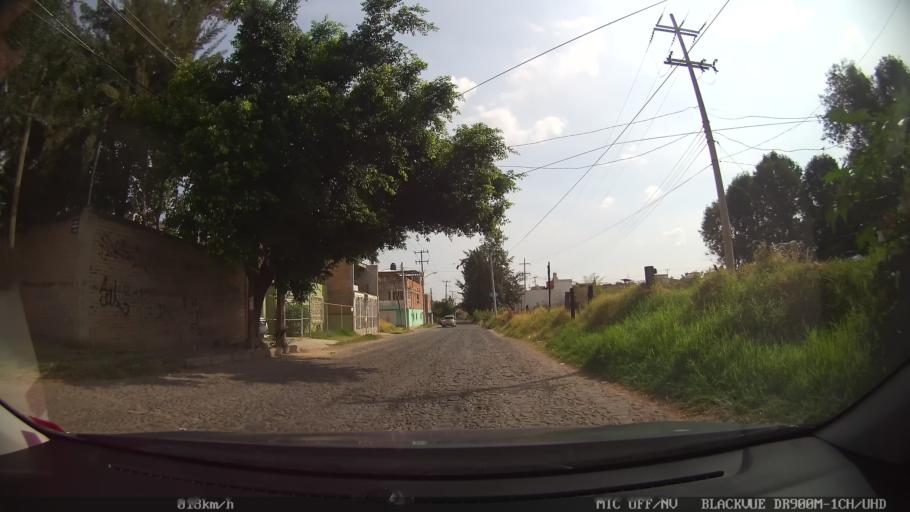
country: MX
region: Jalisco
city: Tonala
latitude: 20.6483
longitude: -103.2294
